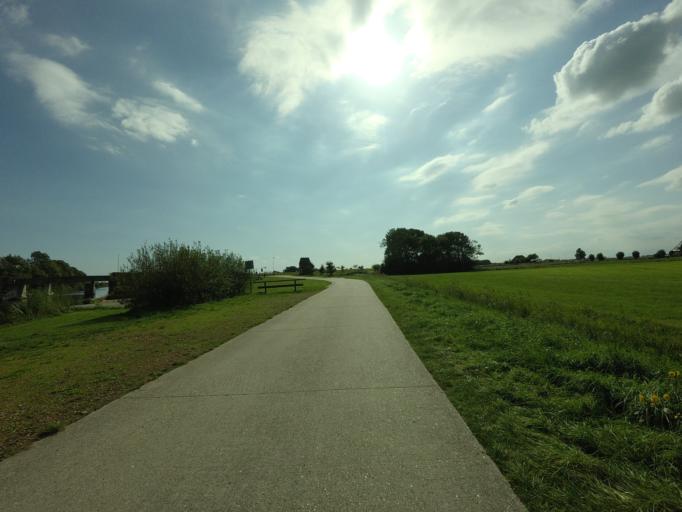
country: NL
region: Friesland
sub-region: Sudwest Fryslan
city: Scharnegoutum
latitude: 53.0771
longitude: 5.6310
